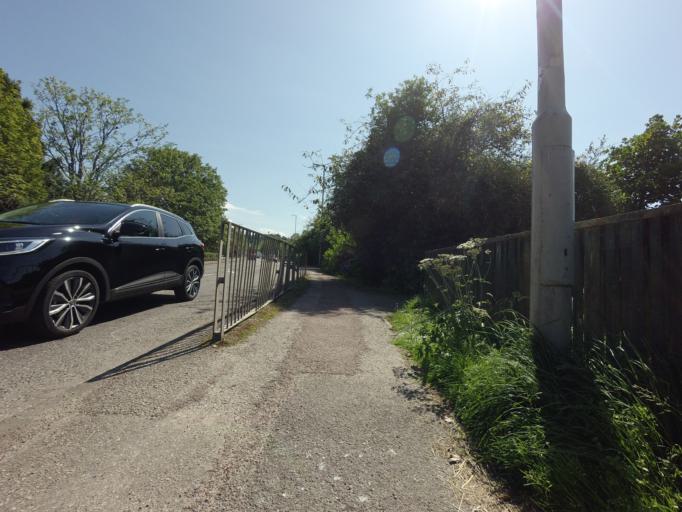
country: GB
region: Scotland
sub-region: Highland
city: Dingwall
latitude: 57.5991
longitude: -4.4327
